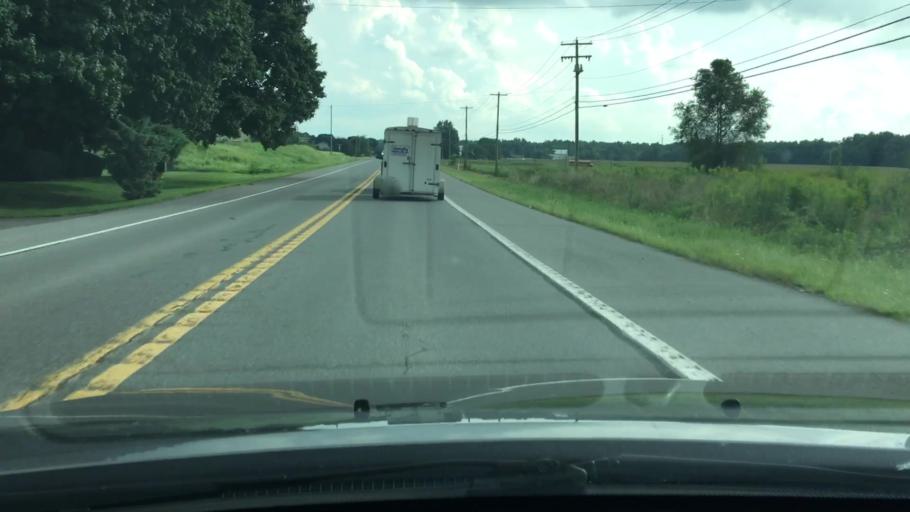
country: US
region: Pennsylvania
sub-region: Franklin County
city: Scotland
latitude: 39.9488
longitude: -77.5840
